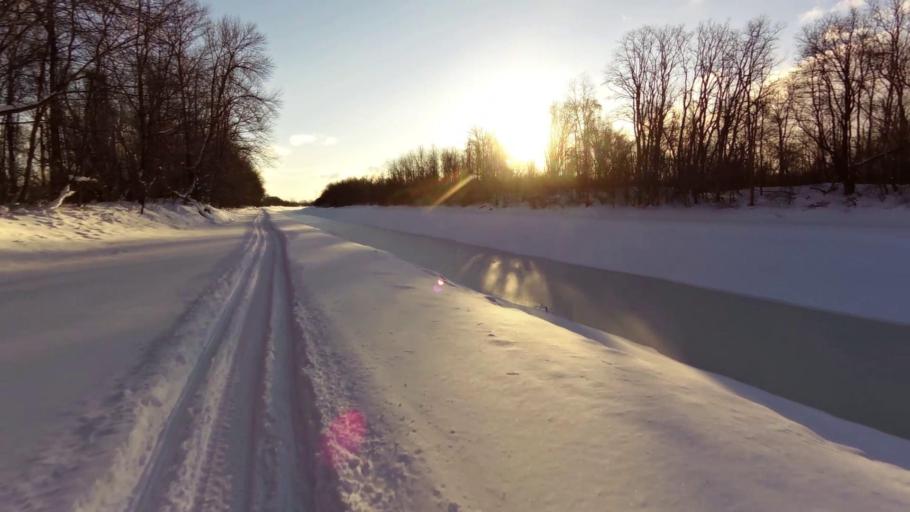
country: US
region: New York
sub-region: Orleans County
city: Medina
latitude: 43.2311
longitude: -78.3682
